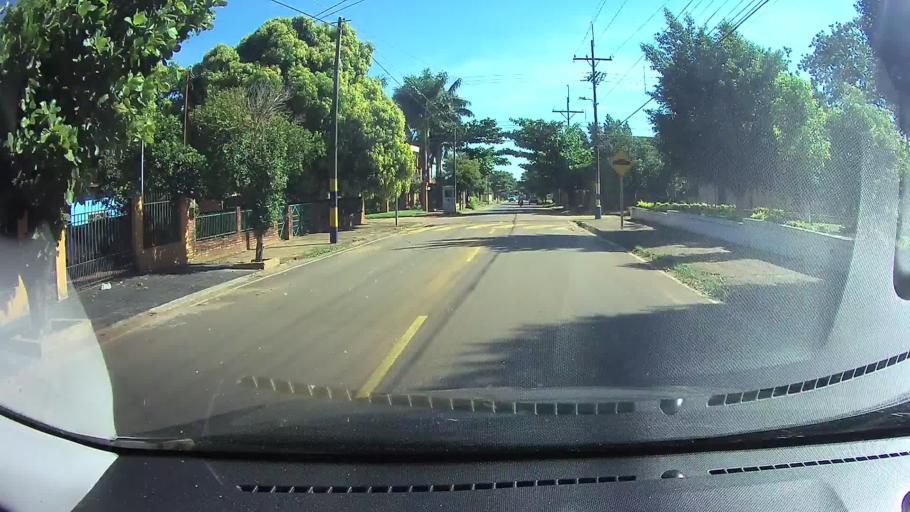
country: PY
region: Central
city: San Lorenzo
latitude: -25.2734
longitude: -57.5037
